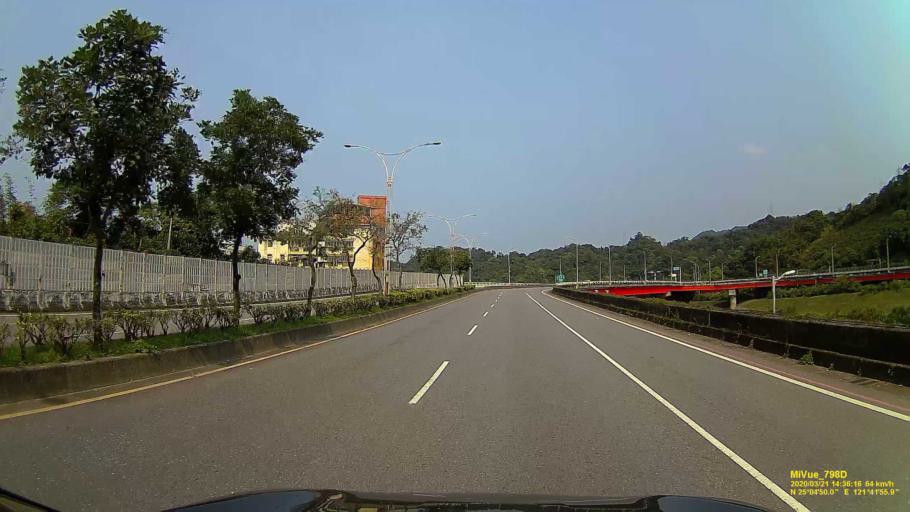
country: TW
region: Taiwan
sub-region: Keelung
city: Keelung
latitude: 25.0805
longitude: 121.6988
